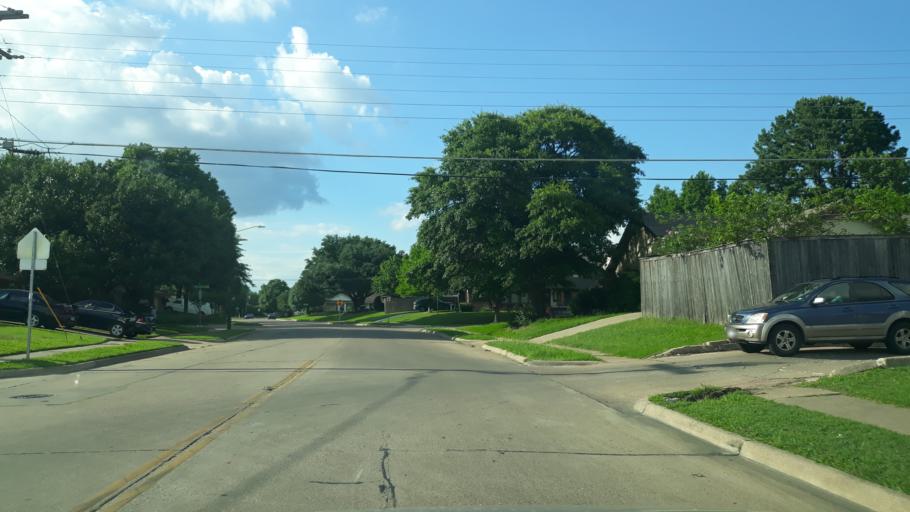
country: US
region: Texas
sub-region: Dallas County
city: Irving
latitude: 32.8577
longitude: -97.0016
